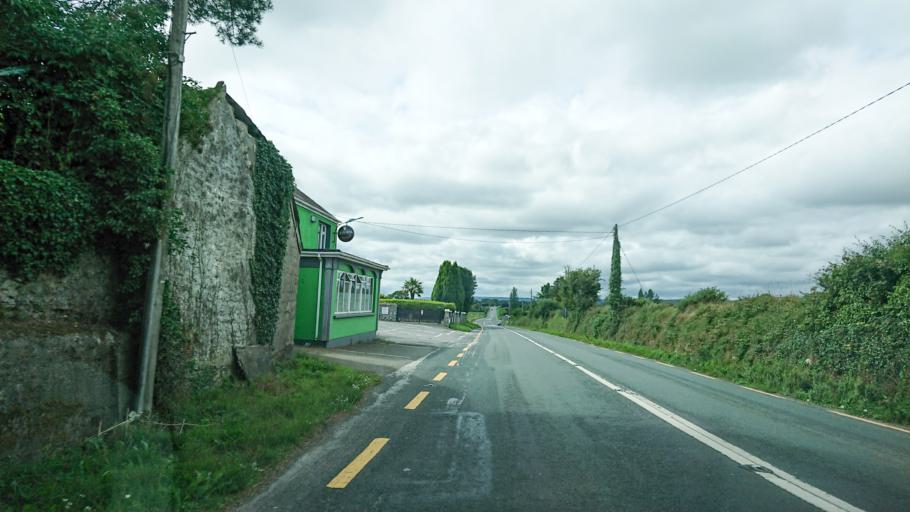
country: IE
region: Munster
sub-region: Waterford
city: Dungarvan
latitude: 52.1244
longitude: -7.7702
